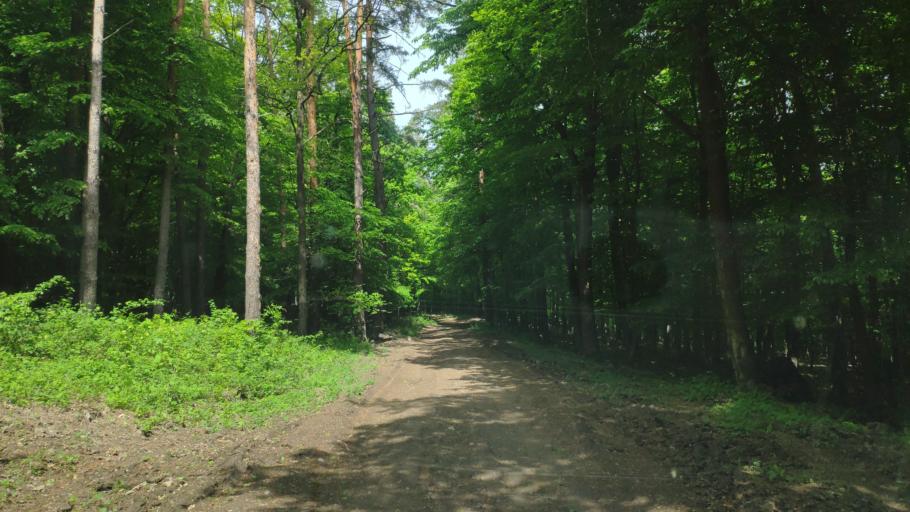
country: SK
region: Kosicky
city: Secovce
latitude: 48.7111
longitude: 21.5818
